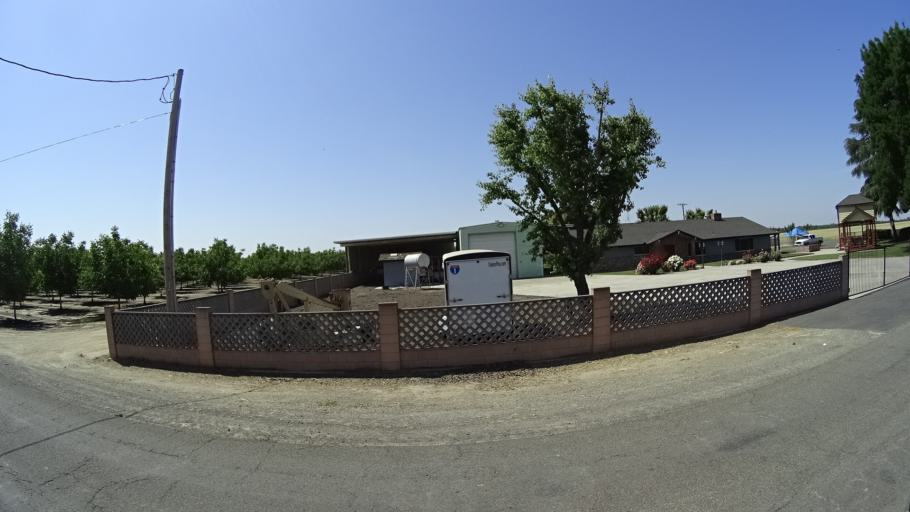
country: US
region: California
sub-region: Kings County
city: Lucerne
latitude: 36.3717
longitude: -119.6092
